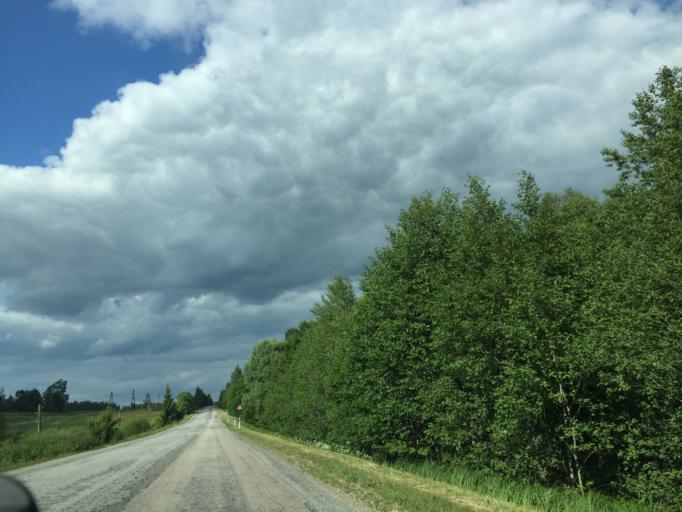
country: LV
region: Skriveri
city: Skriveri
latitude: 56.8146
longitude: 25.1164
